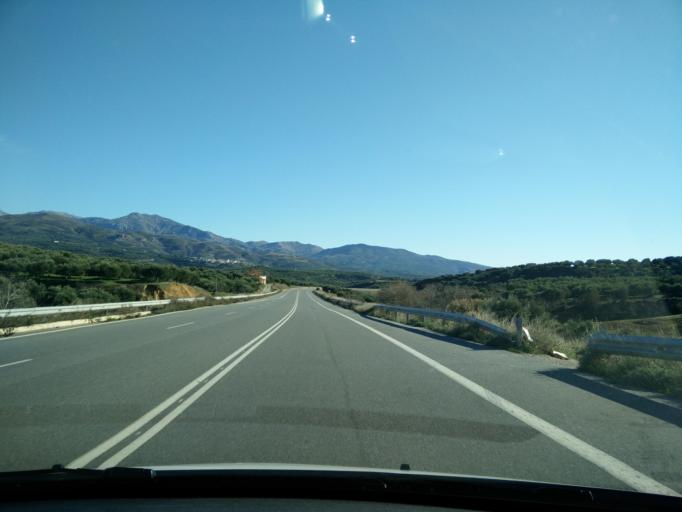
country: GR
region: Crete
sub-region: Nomos Irakleiou
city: Arkalochori
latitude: 35.1197
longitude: 25.2859
